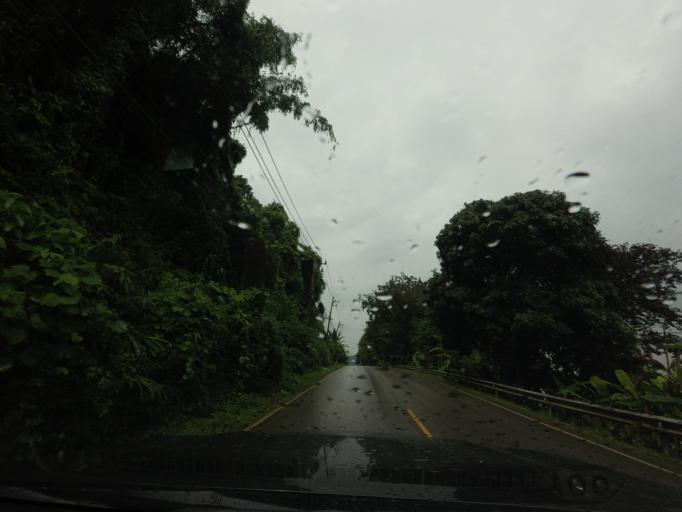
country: TH
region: Nong Khai
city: Sangkhom
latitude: 18.1664
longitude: 102.1742
